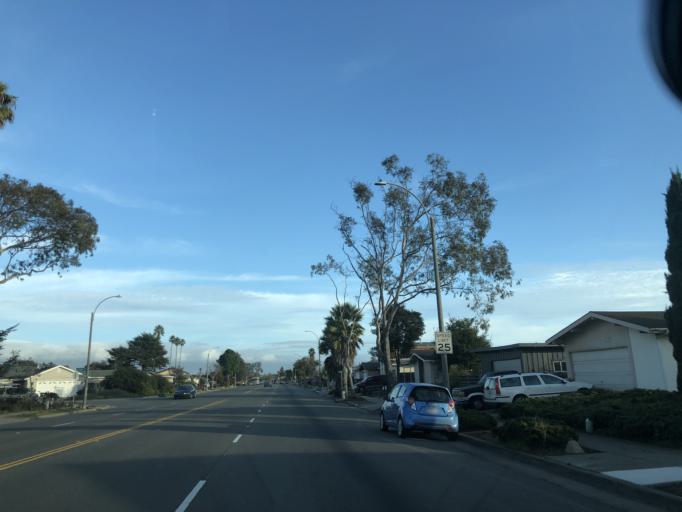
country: US
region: California
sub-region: Alameda County
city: Alameda
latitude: 37.7643
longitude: -122.2655
